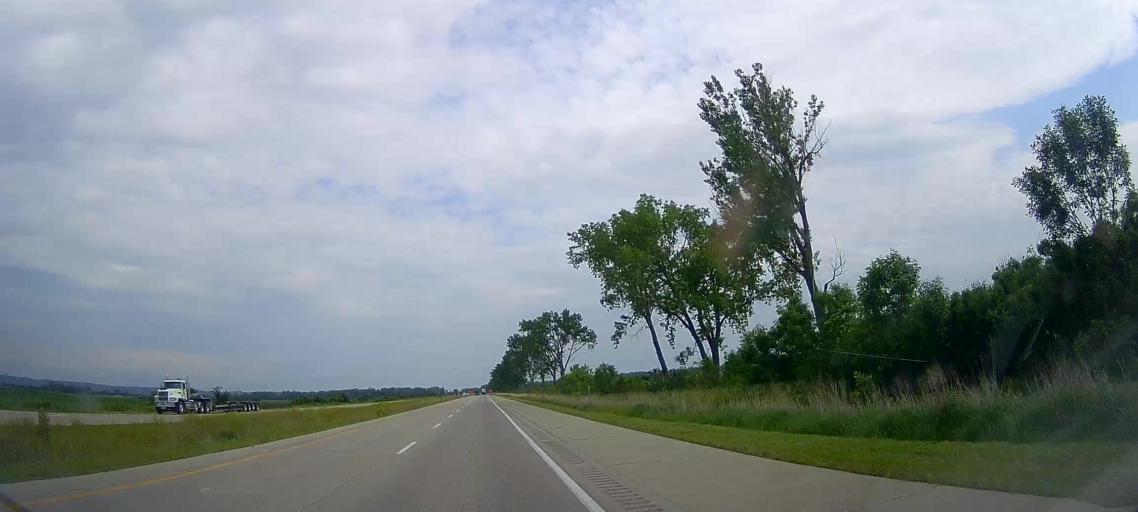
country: US
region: Nebraska
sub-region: Burt County
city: Tekamah
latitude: 41.8346
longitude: -96.0839
